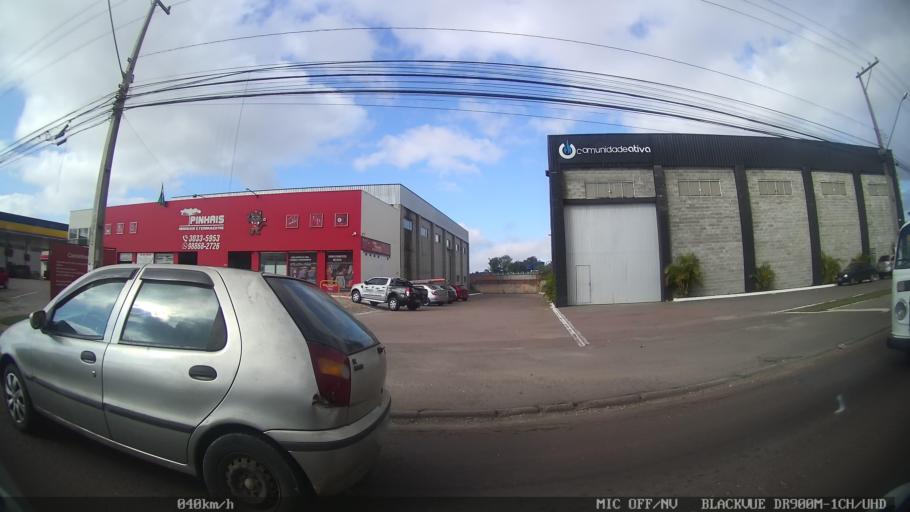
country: BR
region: Parana
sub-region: Pinhais
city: Pinhais
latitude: -25.4112
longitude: -49.1898
